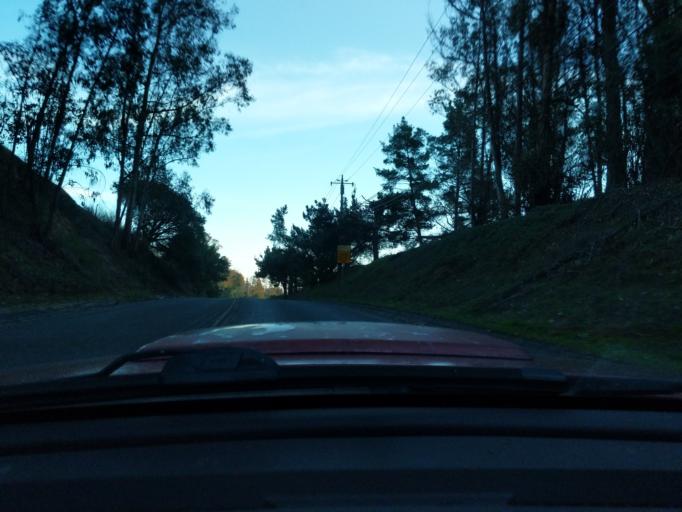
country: US
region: California
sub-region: Monterey County
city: Prunedale
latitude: 36.8294
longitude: -121.6671
